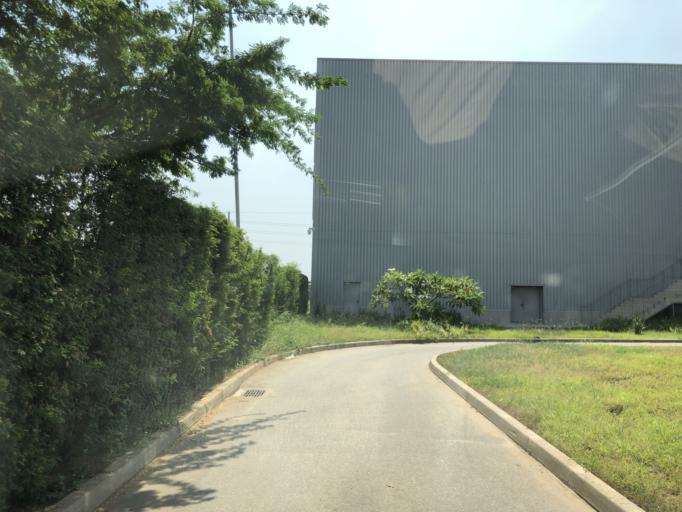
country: AO
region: Luanda
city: Luanda
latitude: -8.8972
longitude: 13.2246
